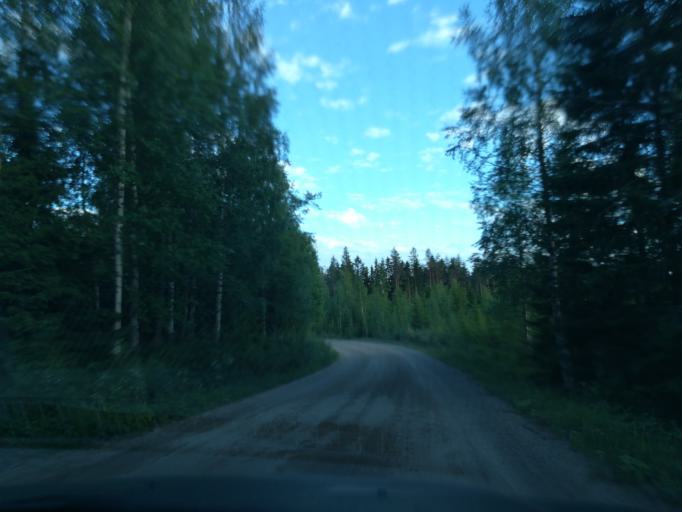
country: FI
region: Southern Savonia
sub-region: Mikkeli
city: Puumala
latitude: 61.6189
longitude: 28.1119
